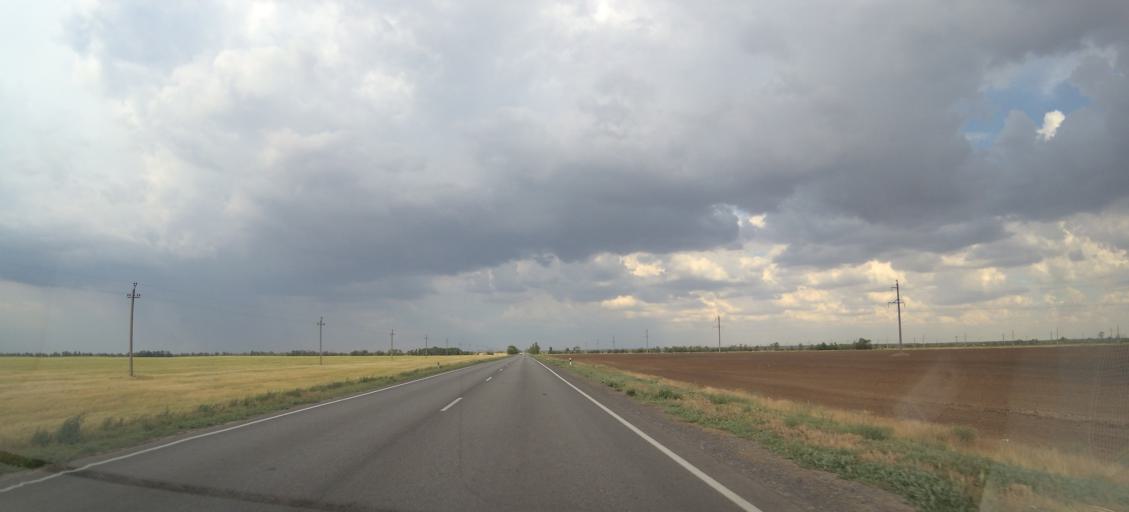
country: RU
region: Rostov
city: Zimovniki
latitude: 47.1230
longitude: 42.3974
